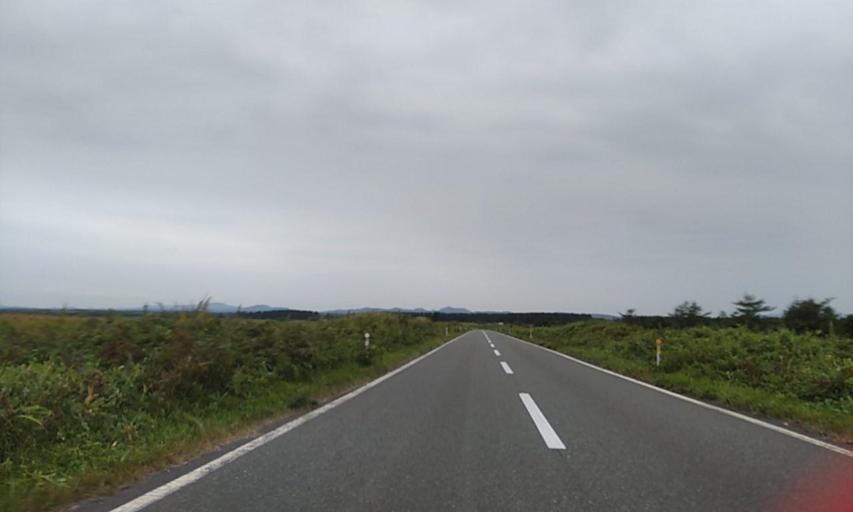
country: JP
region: Hokkaido
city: Makubetsu
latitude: 45.2373
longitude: 142.2678
